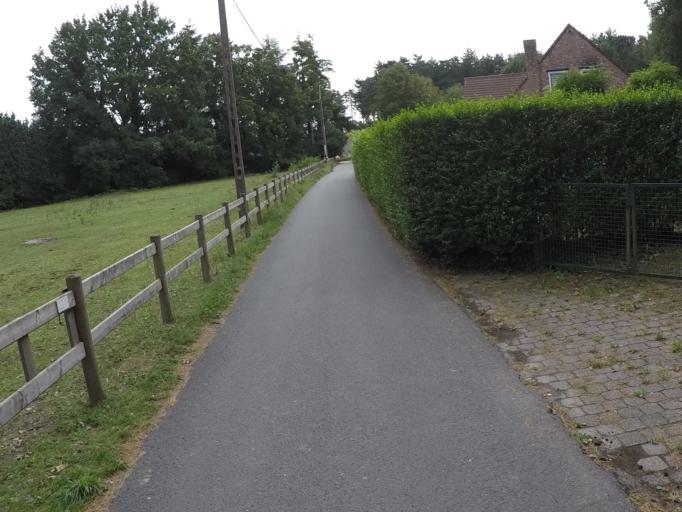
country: BE
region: Flanders
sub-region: Provincie Antwerpen
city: Zandhoven
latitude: 51.2191
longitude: 4.6589
